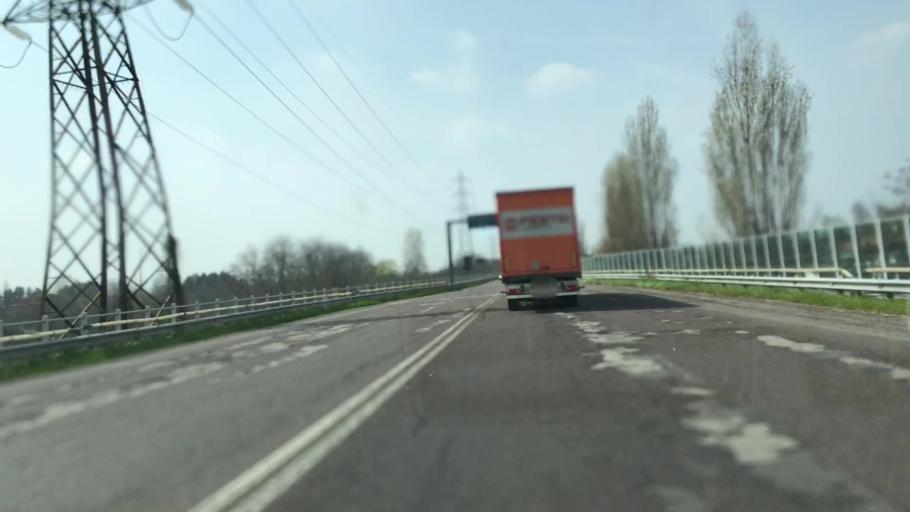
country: IT
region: Lombardy
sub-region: Provincia di Mantova
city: Sant'Antonio
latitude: 45.1856
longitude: 10.7840
